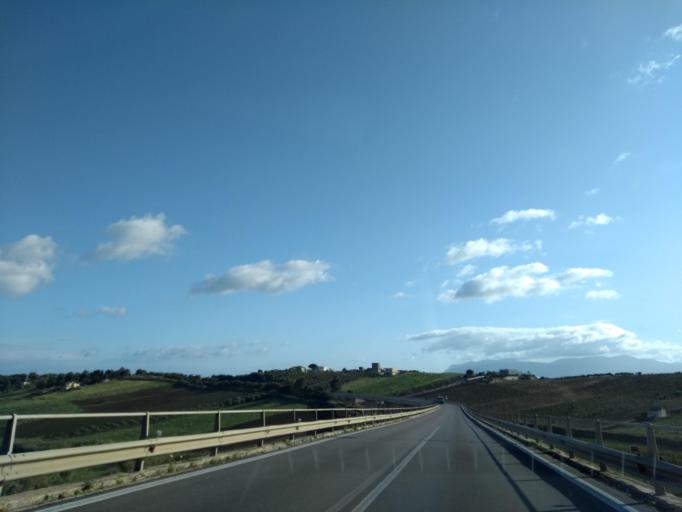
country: IT
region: Sicily
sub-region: Trapani
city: Alcamo
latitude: 38.0052
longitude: 12.9595
